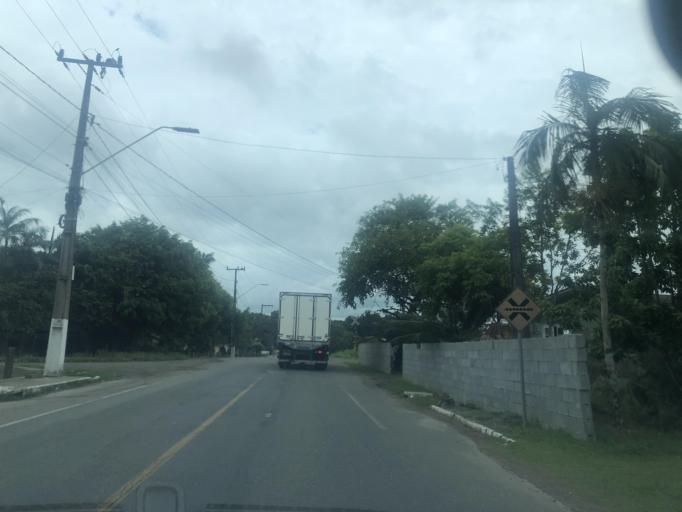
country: BR
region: Santa Catarina
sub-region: Joinville
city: Joinville
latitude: -26.3806
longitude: -48.7255
